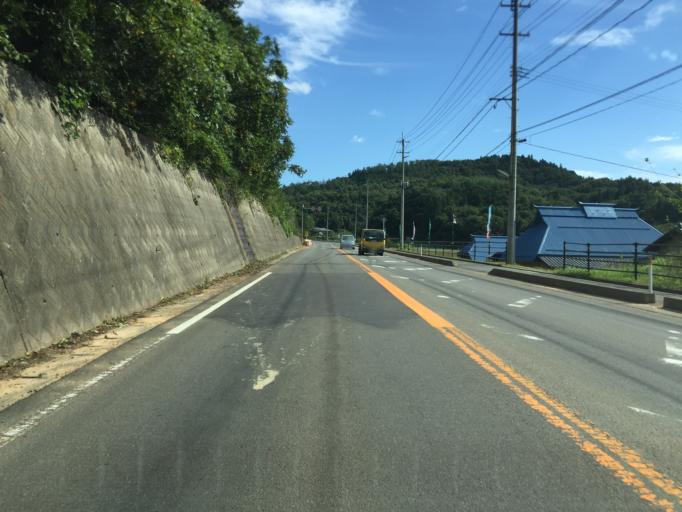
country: JP
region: Fukushima
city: Hobaramachi
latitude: 37.7908
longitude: 140.5747
